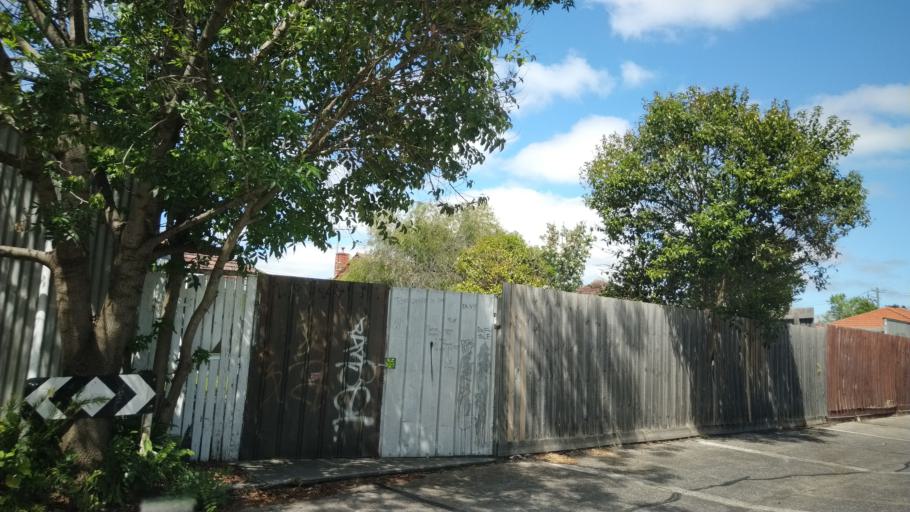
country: AU
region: Victoria
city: Hughesdale
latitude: -37.9019
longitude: 145.0779
